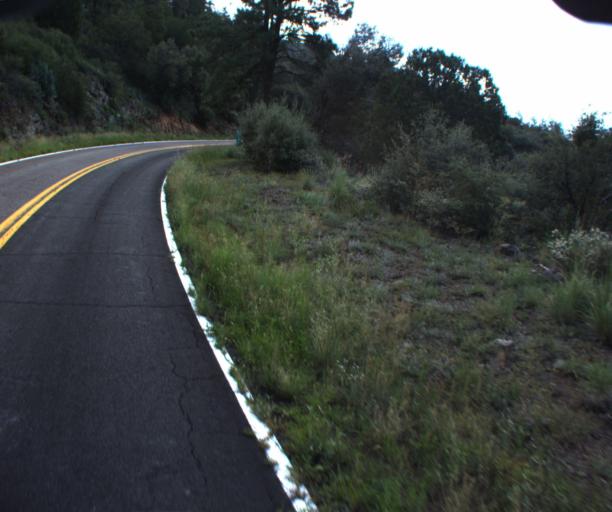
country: US
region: Arizona
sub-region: Greenlee County
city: Morenci
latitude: 33.4854
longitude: -109.3648
